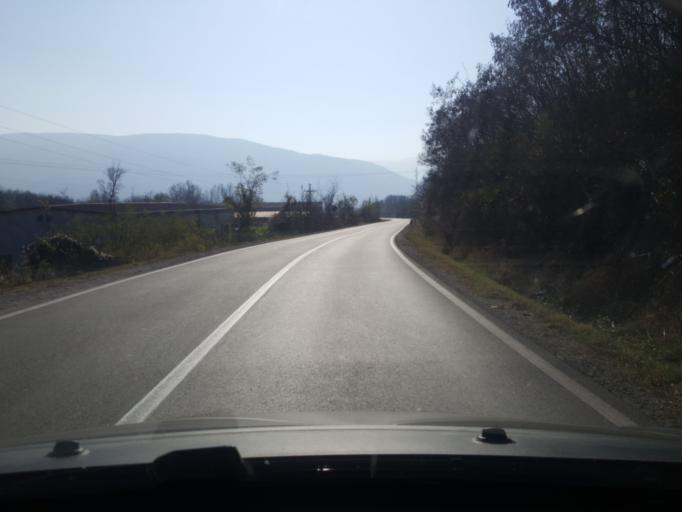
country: RS
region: Central Serbia
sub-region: Nisavski Okrug
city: Niska Banja
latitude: 43.3251
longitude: 22.0217
